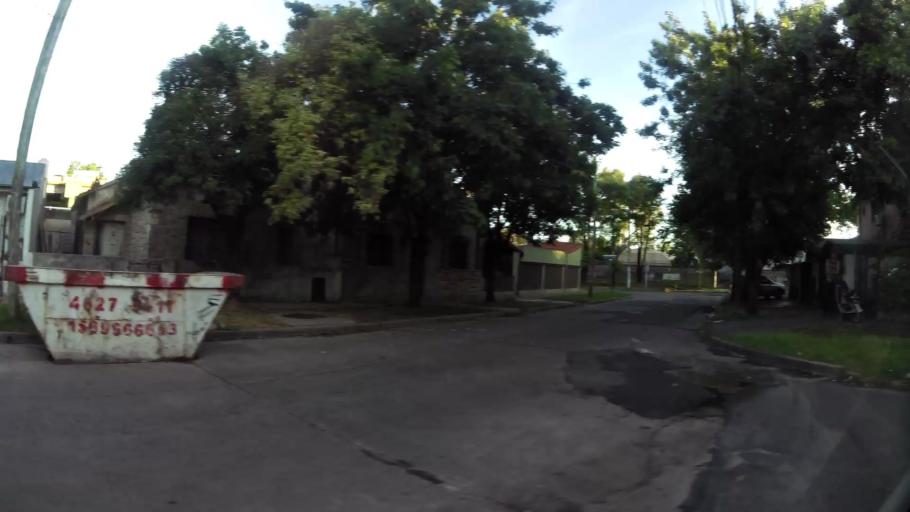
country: AR
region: Buenos Aires
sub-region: Partido de Moron
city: Moron
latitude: -34.6486
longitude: -58.6294
